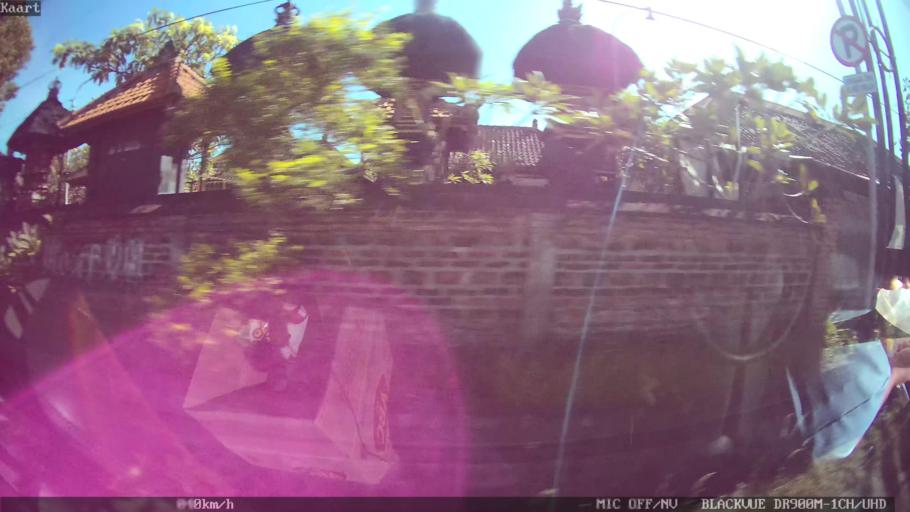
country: ID
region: Bali
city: Banjar Karangsuling
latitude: -8.6208
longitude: 115.1842
